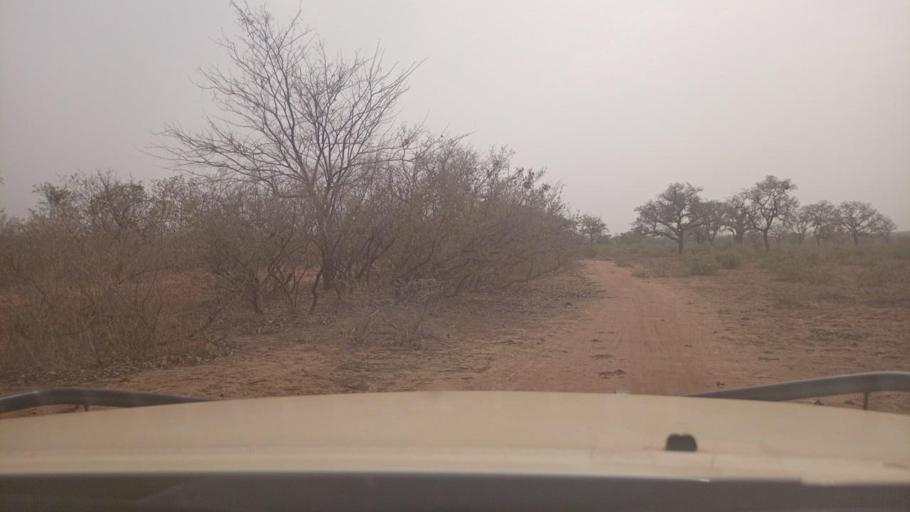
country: BF
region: Boucle du Mouhoun
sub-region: Province des Banwa
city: Salanso
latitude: 12.1614
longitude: -4.2412
